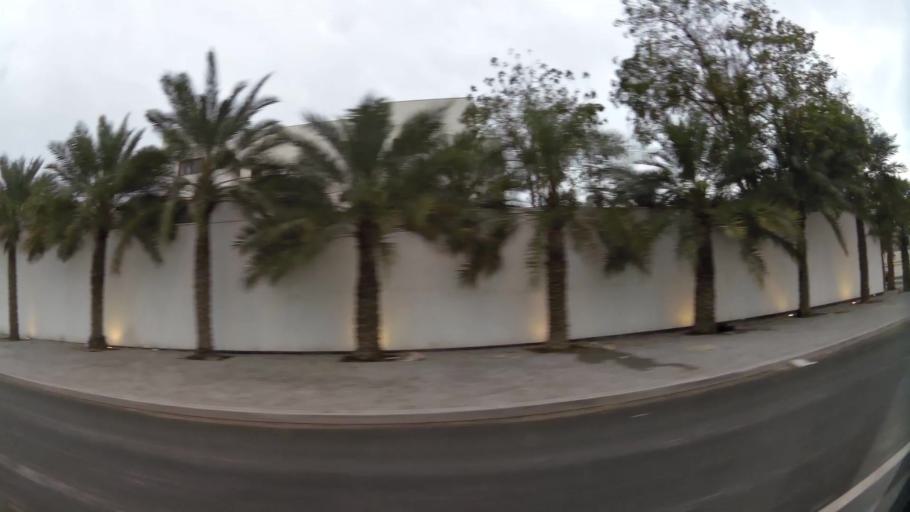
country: BH
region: Northern
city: Madinat `Isa
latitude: 26.1507
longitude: 50.5349
